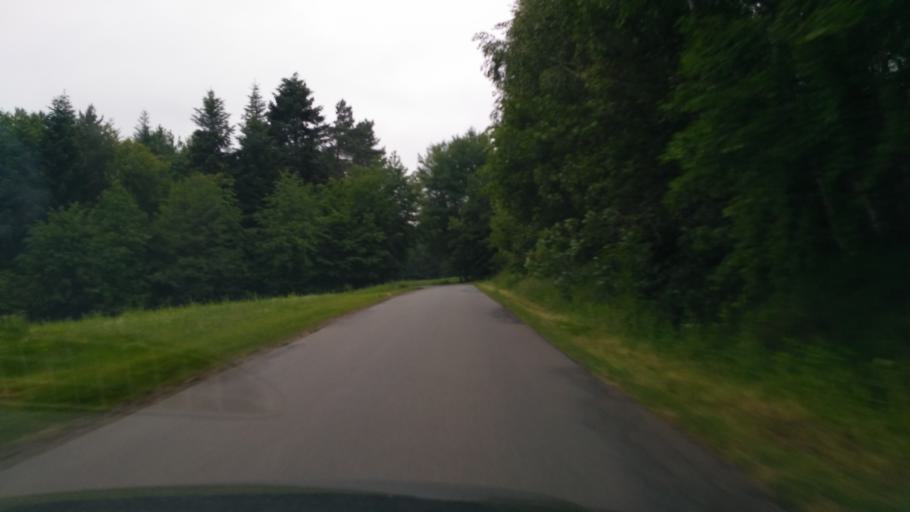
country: PL
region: Subcarpathian Voivodeship
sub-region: Powiat brzozowski
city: Orzechowka
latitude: 49.7273
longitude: 21.9242
